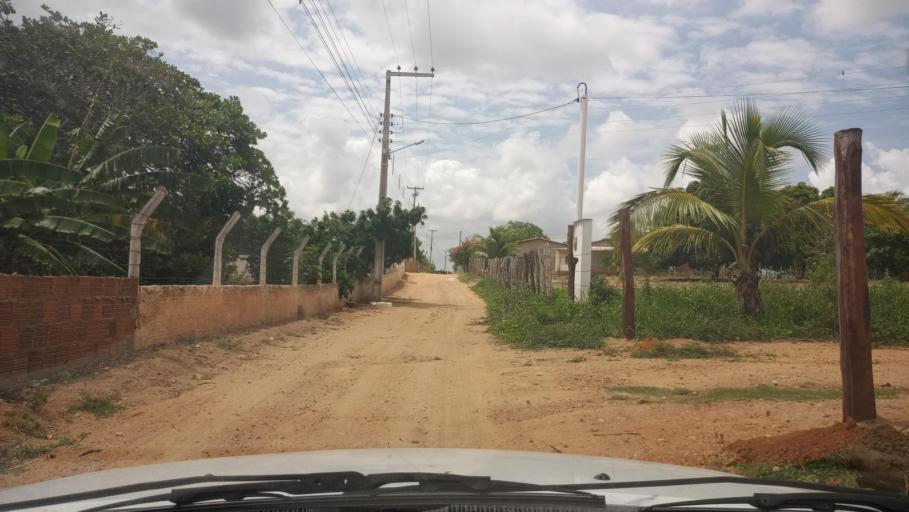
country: BR
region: Rio Grande do Norte
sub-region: Sao Paulo Do Potengi
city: Sao Paulo do Potengi
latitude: -5.9148
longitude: -35.6948
